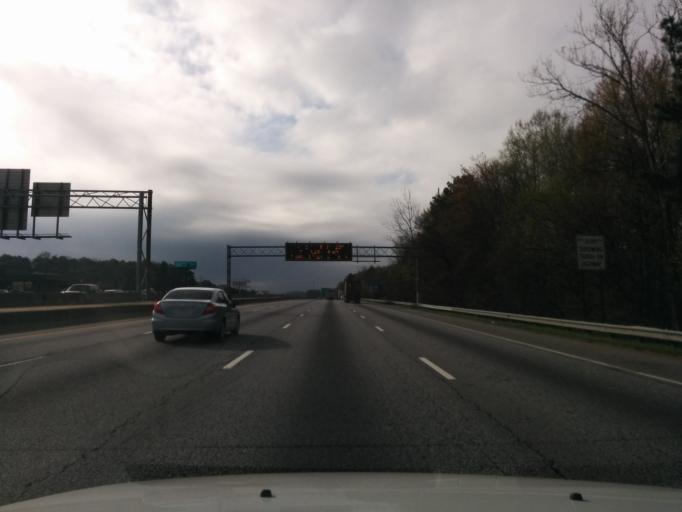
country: US
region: Georgia
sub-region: Clayton County
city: Forest Park
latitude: 33.6044
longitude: -84.3938
